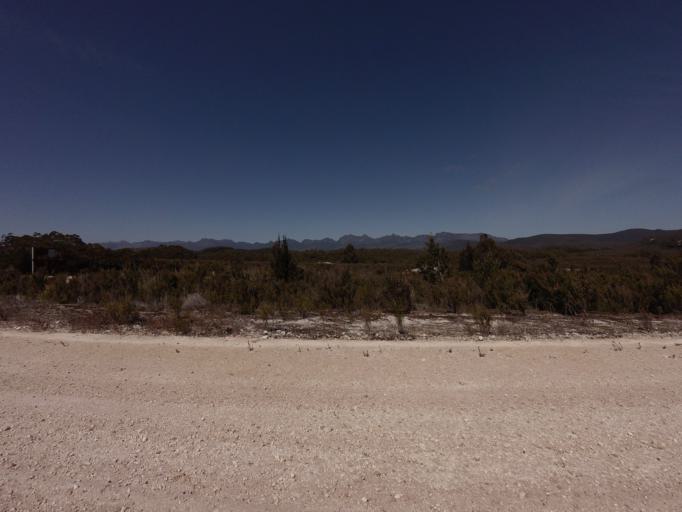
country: AU
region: Tasmania
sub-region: Huon Valley
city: Geeveston
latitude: -43.0312
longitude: 146.3042
